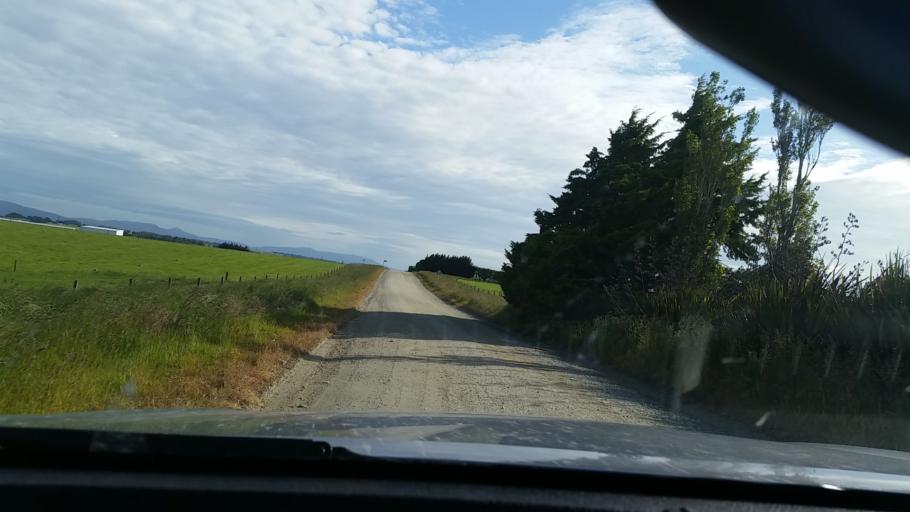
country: NZ
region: Southland
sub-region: Gore District
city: Gore
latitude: -46.2758
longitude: 168.7116
